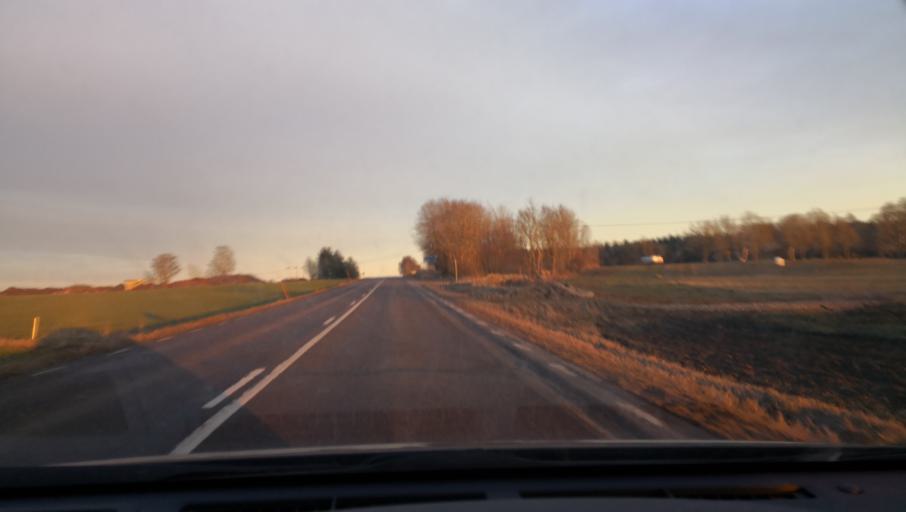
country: SE
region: OErebro
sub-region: Orebro Kommun
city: Vintrosa
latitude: 59.2443
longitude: 14.9674
